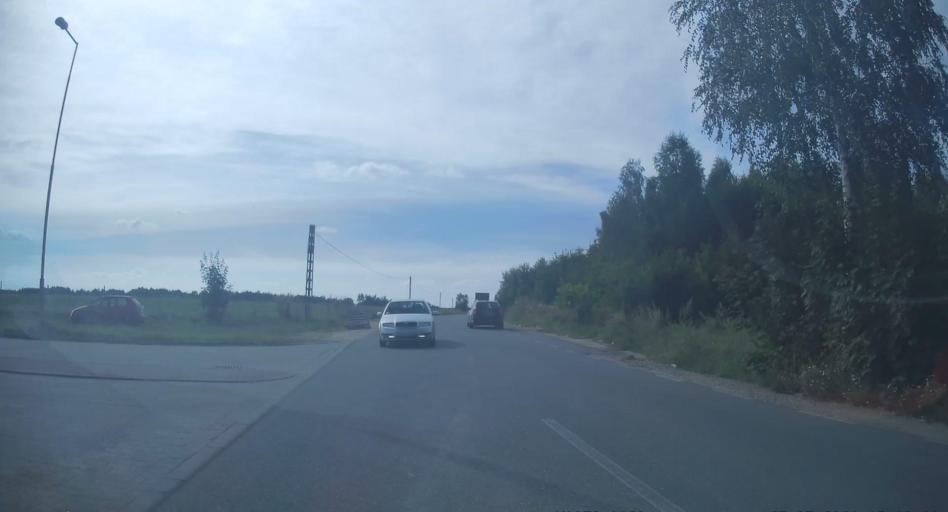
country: PL
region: Lodz Voivodeship
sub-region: Powiat rawski
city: Rawa Mazowiecka
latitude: 51.7028
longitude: 20.2266
